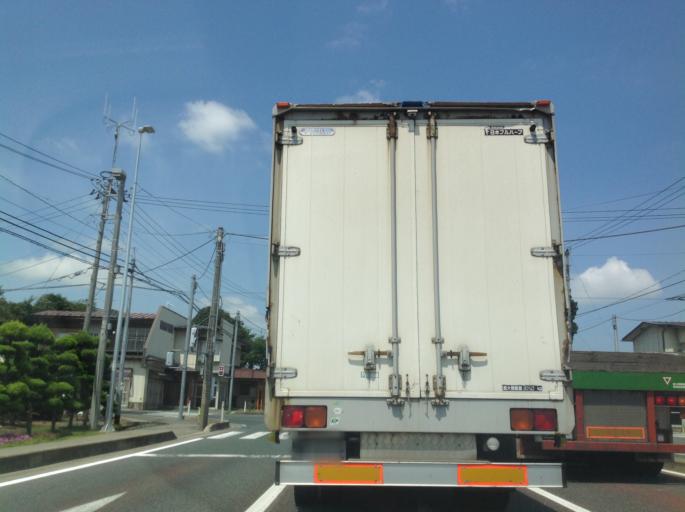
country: JP
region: Iwate
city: Kitakami
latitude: 39.3202
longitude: 141.1120
